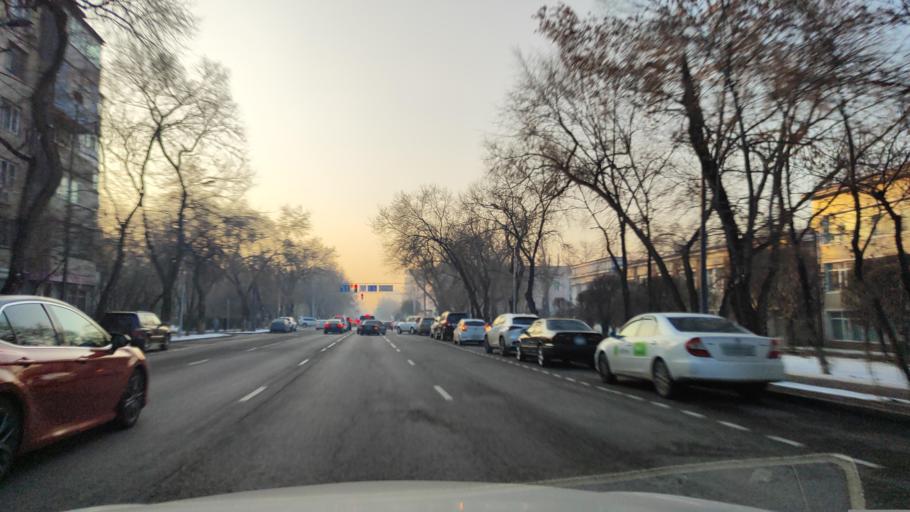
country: KZ
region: Almaty Qalasy
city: Almaty
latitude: 43.2536
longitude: 76.9519
